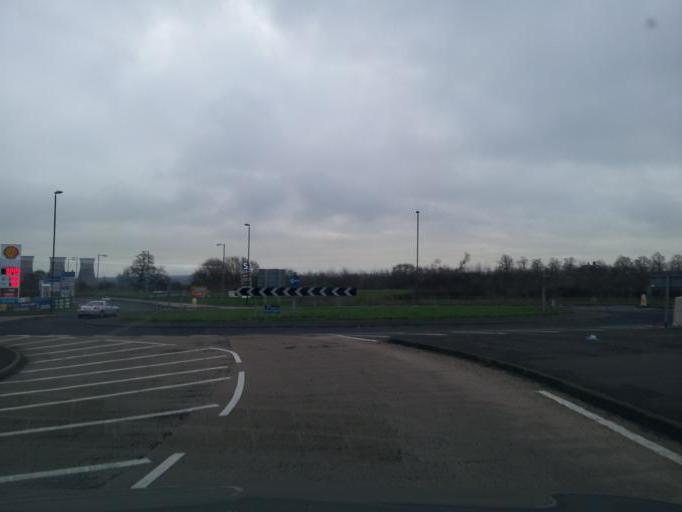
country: GB
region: England
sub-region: Derbyshire
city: Findern
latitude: 52.8638
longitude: -1.5659
